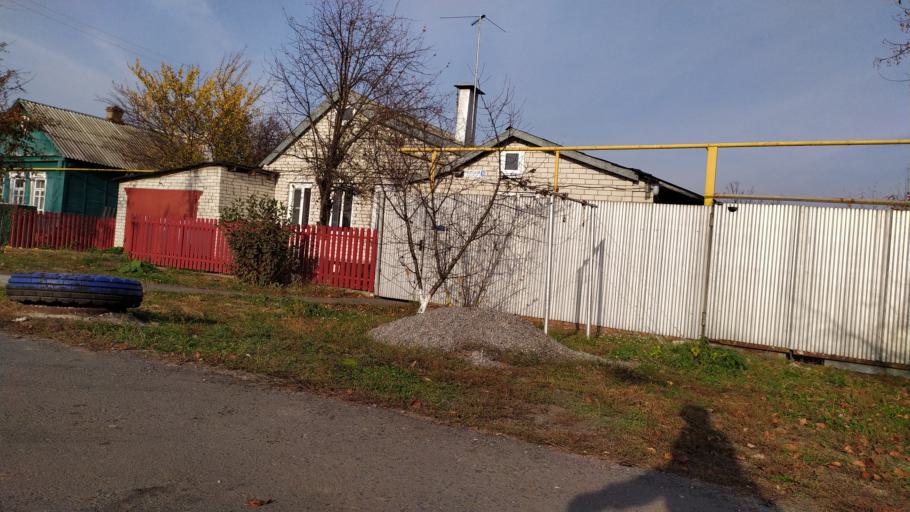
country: RU
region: Kursk
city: Kursk
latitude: 51.6456
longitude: 36.1452
